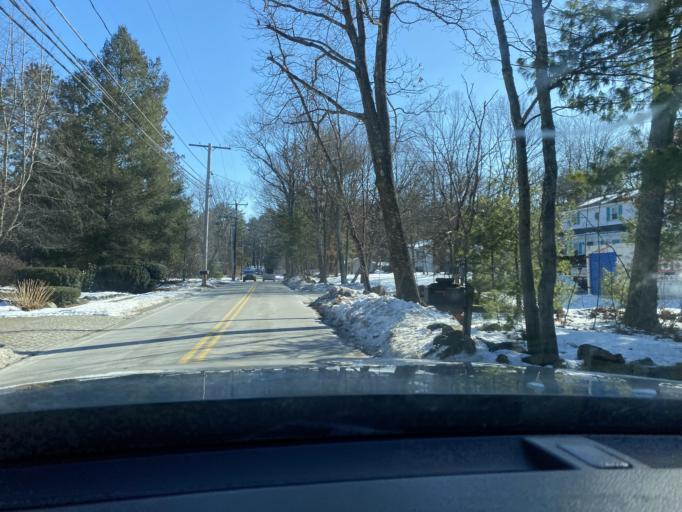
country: US
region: Massachusetts
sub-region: Norfolk County
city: Walpole
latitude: 42.1633
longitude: -71.2566
